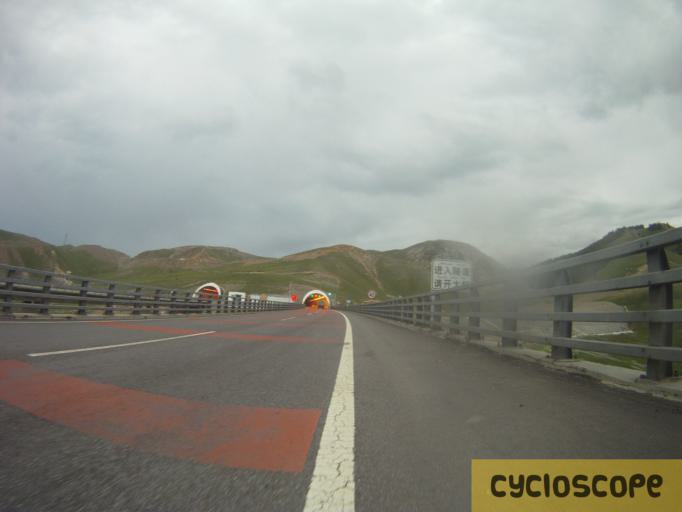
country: CN
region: Xinjiang Uygur Zizhiqu
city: Yengiyar
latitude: 44.4834
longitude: 81.1535
